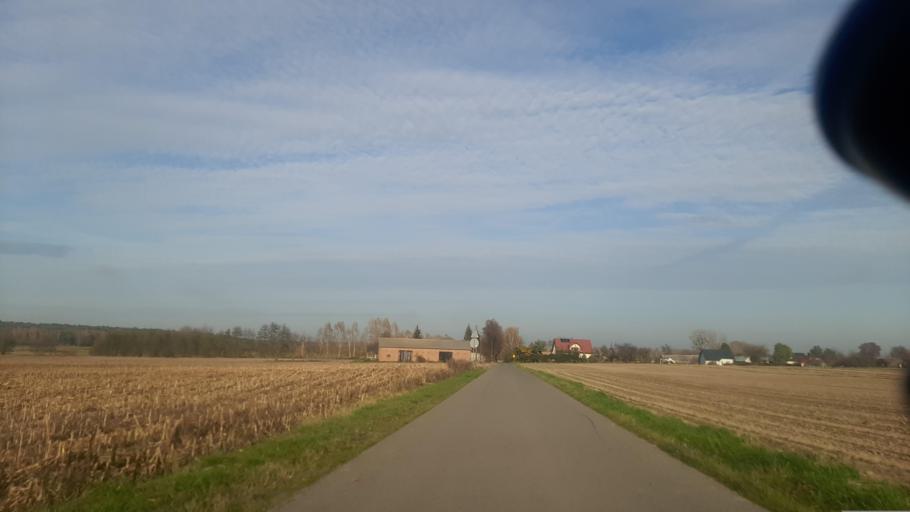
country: PL
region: Lublin Voivodeship
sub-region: Powiat pulawski
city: Markuszow
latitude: 51.3845
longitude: 22.2891
